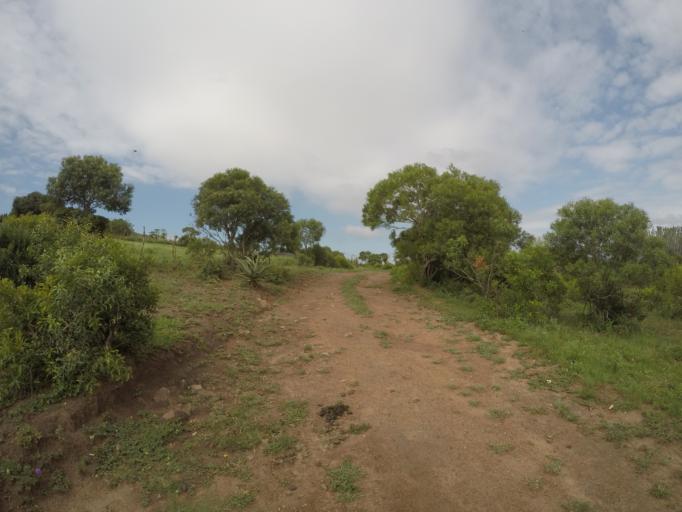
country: ZA
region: KwaZulu-Natal
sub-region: uThungulu District Municipality
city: Empangeni
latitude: -28.6255
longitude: 31.8633
